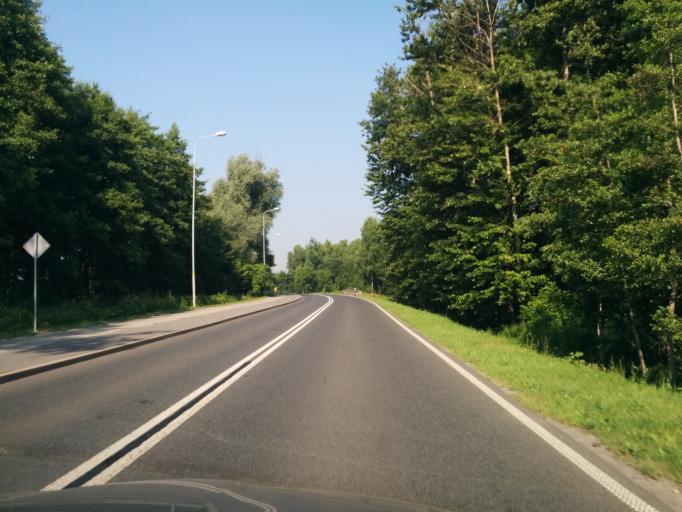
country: PL
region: Silesian Voivodeship
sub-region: Powiat gliwicki
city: Paniowki
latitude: 50.2655
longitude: 18.8039
